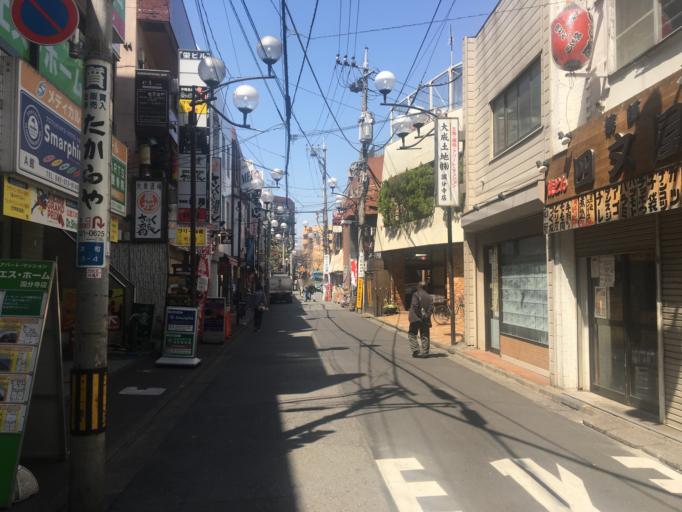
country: JP
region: Tokyo
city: Kokubunji
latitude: 35.7011
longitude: 139.4800
